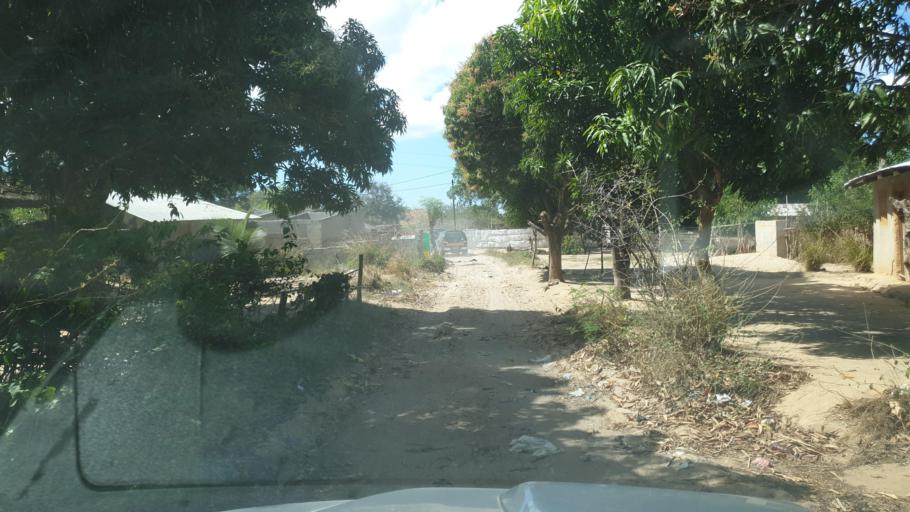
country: MZ
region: Nampula
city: Nacala
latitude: -14.5683
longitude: 40.7037
